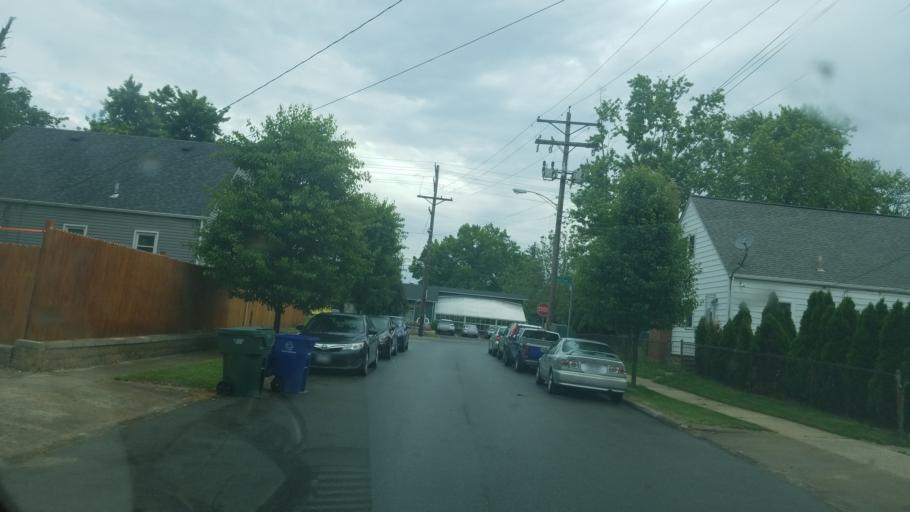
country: US
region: Ohio
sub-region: Franklin County
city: Minerva Park
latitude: 40.0318
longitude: -82.9830
